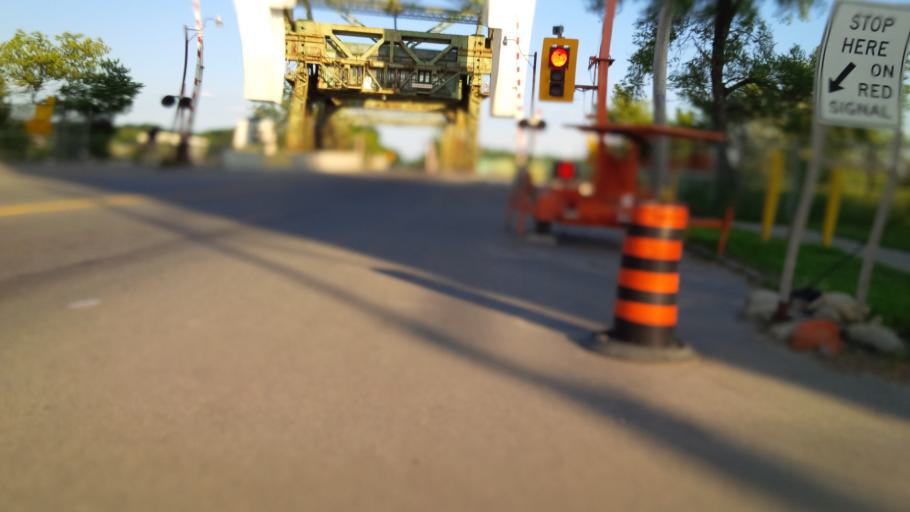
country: CA
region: Ontario
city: Toronto
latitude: 43.6419
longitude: -79.3498
